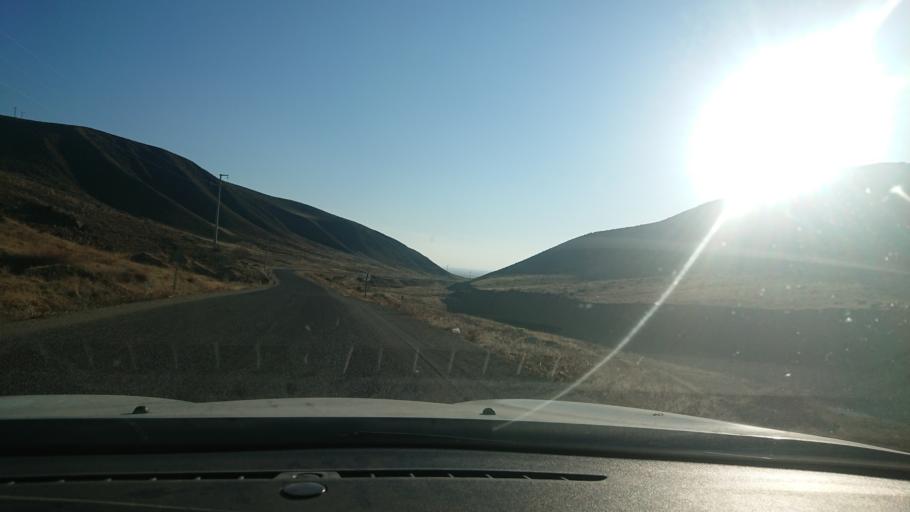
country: TR
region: Aksaray
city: Acipinar
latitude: 38.6897
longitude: 33.7441
